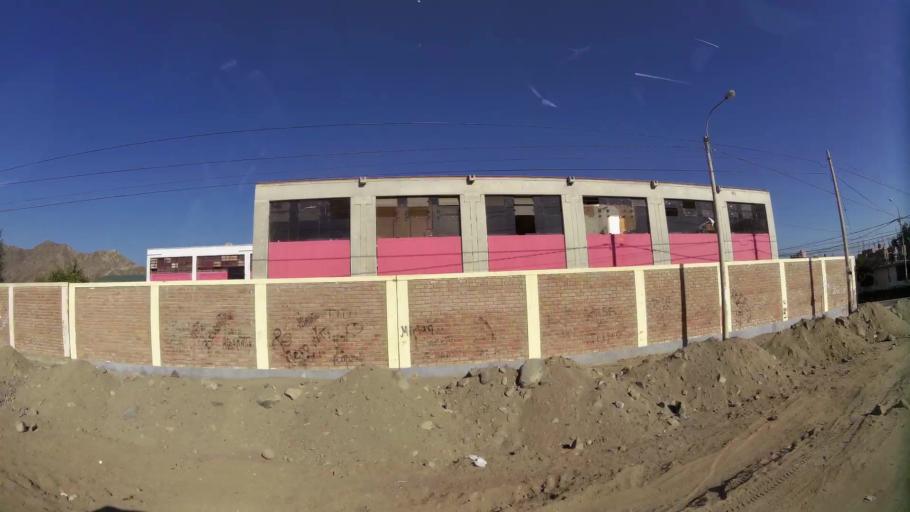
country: PE
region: Ica
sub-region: Provincia de Ica
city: La Tinguina
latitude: -14.0466
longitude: -75.6966
